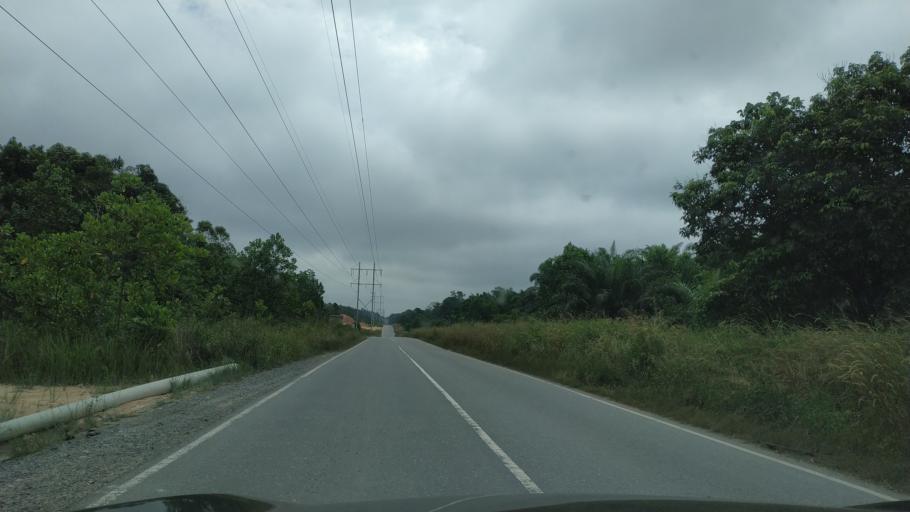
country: ID
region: Riau
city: Pekanbaru
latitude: 0.6435
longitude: 101.6768
